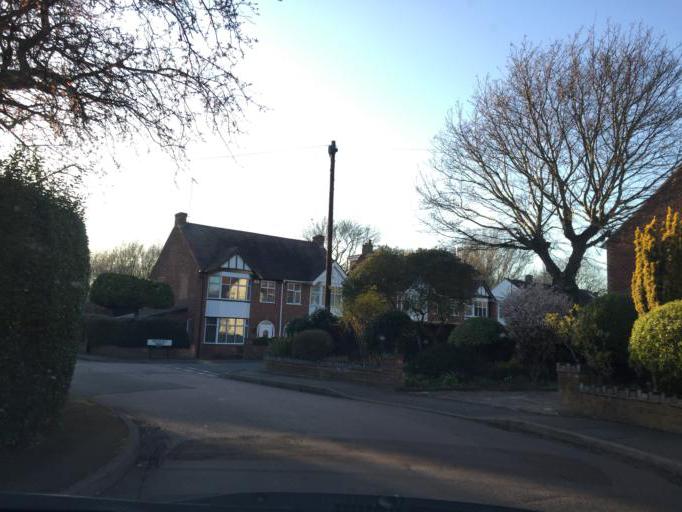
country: GB
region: England
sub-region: Warwickshire
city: Ryton on Dunsmore
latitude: 52.4024
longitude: -1.4567
